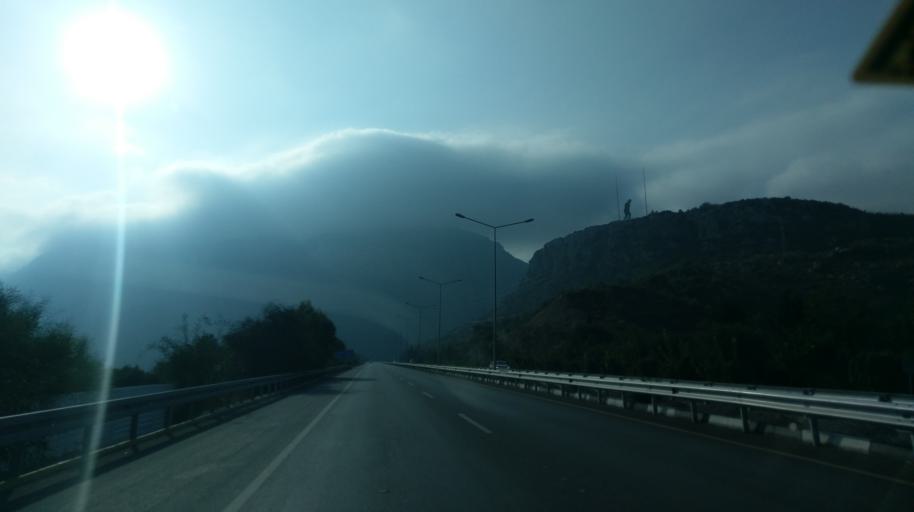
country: CY
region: Keryneia
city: Kyrenia
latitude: 35.3172
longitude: 33.3223
